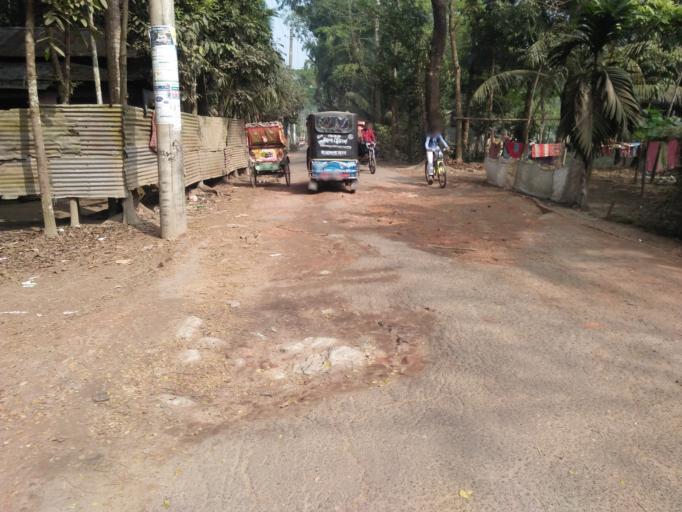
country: BD
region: Barisal
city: Bhola
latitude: 22.6776
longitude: 90.6366
